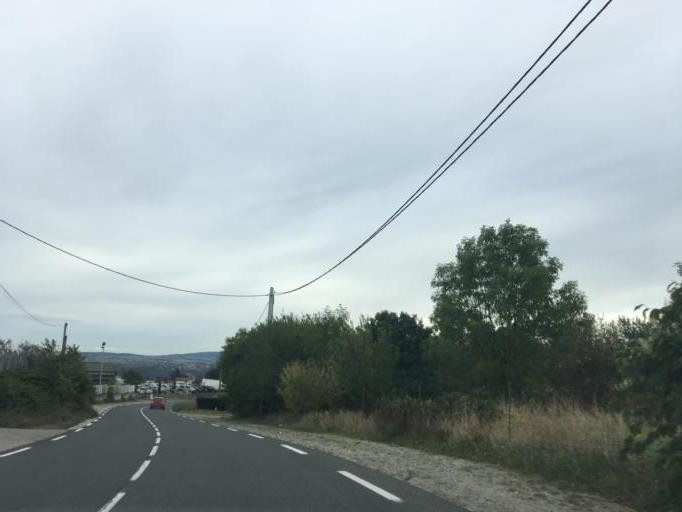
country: FR
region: Rhone-Alpes
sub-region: Departement de la Loire
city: Saint-Joseph
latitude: 45.5470
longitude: 4.6120
